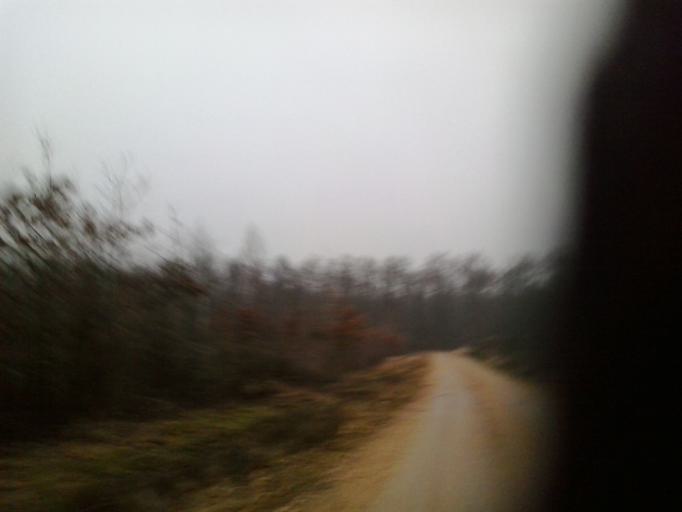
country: HU
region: Vas
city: Sarvar
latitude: 47.1373
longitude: 16.9767
